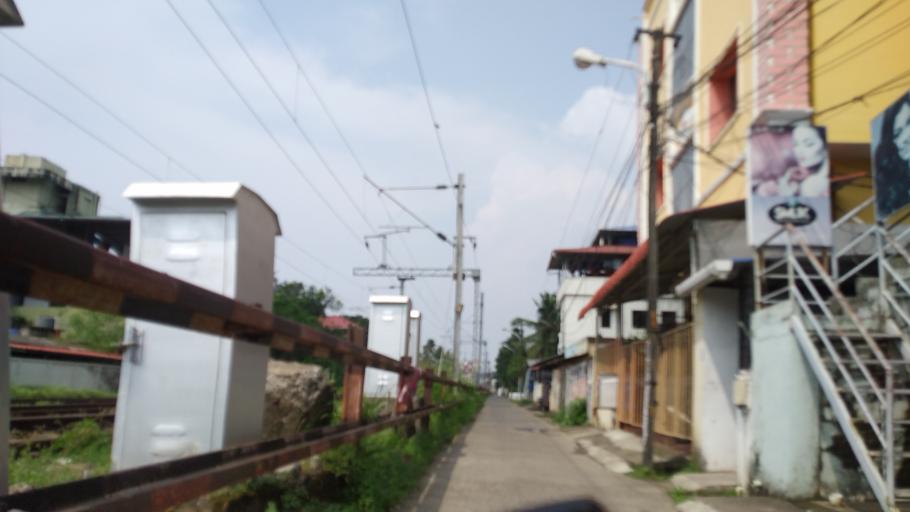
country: IN
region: Kerala
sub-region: Ernakulam
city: Cochin
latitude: 9.9607
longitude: 76.2930
